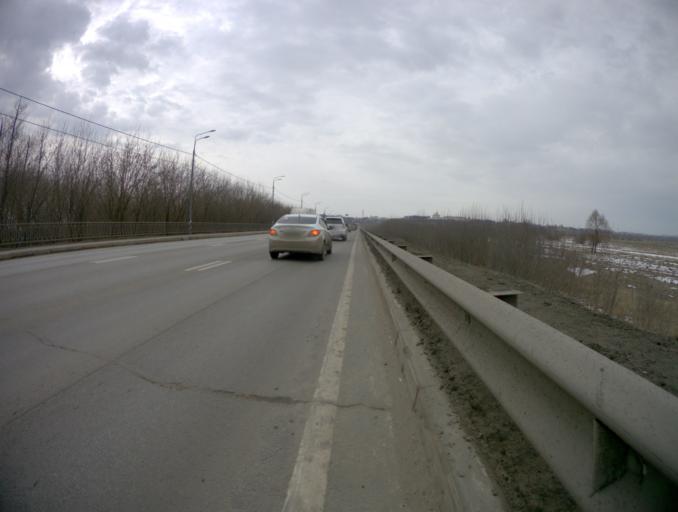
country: RU
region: Vladimir
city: Kommunar
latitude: 56.1132
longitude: 40.4248
